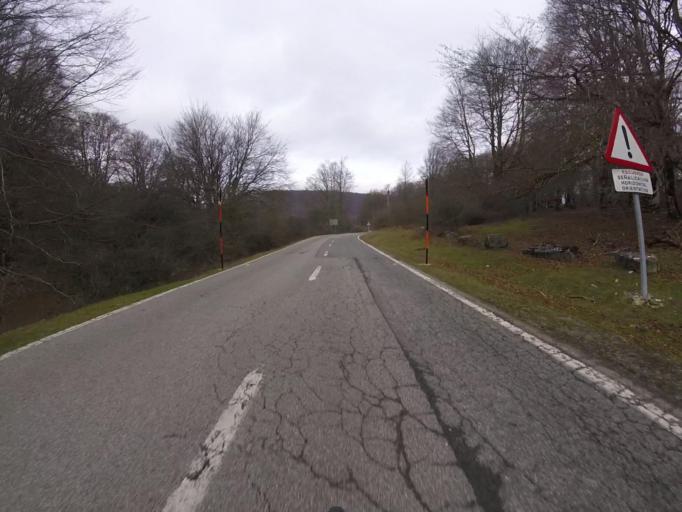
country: ES
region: Navarre
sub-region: Provincia de Navarra
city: Olazagutia
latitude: 42.8464
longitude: -2.1771
